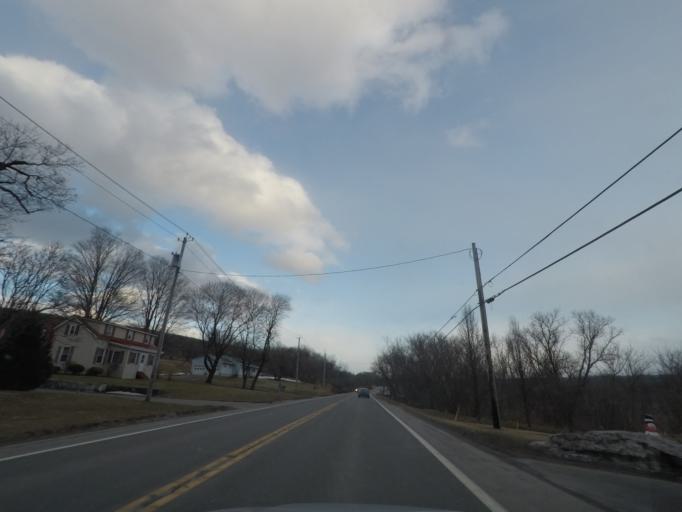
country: US
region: New York
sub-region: Herkimer County
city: Frankfort
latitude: 43.0483
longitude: -75.0657
